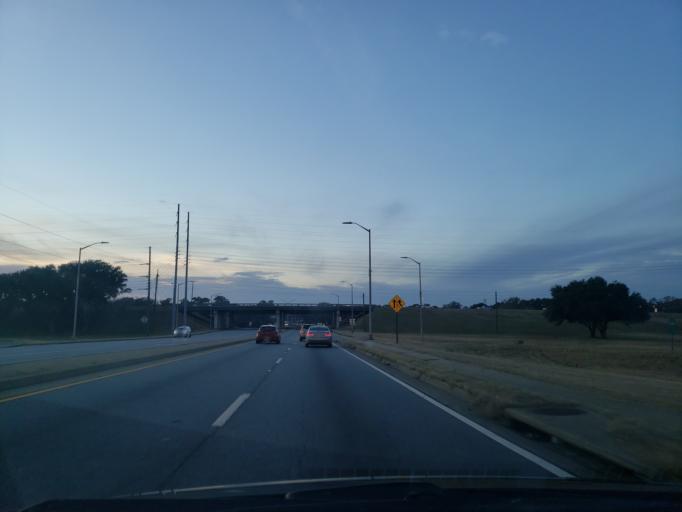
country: US
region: Georgia
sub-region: Dougherty County
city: Albany
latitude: 31.5712
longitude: -84.1094
